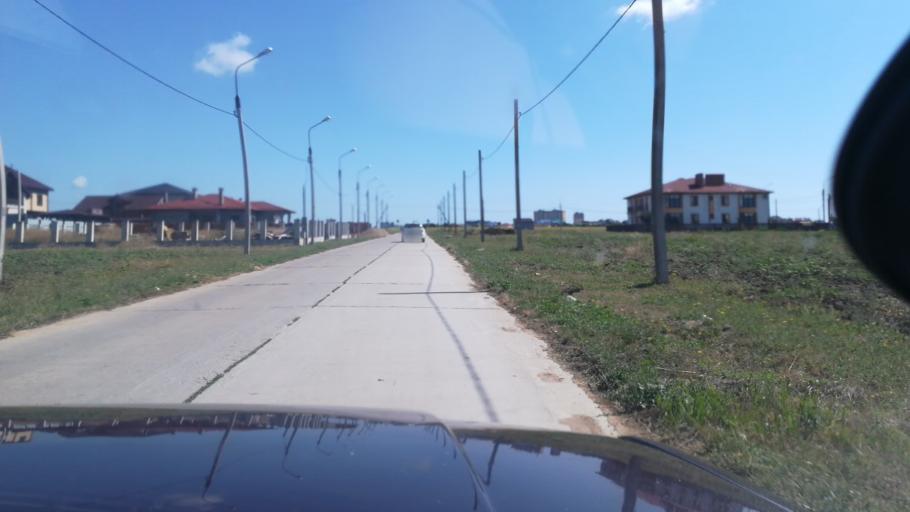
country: RU
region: Krasnodarskiy
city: Vityazevo
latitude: 44.9901
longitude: 37.2755
